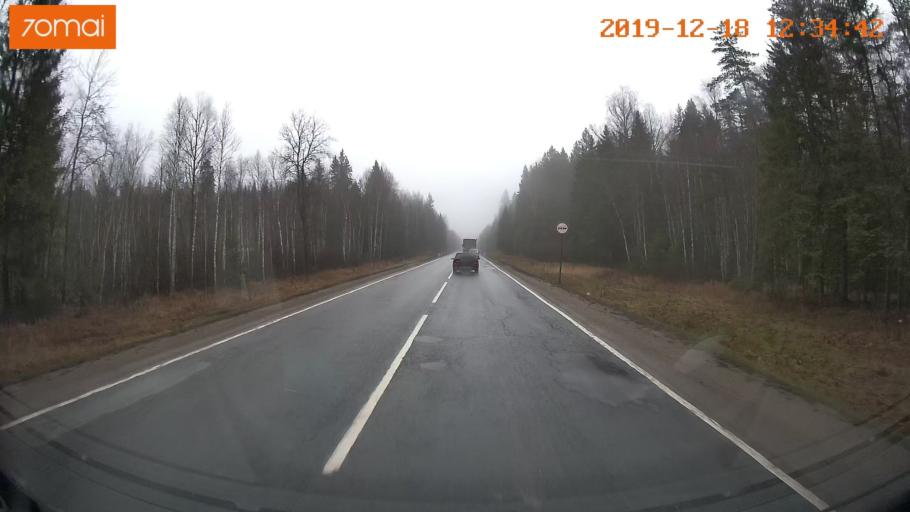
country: RU
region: Moskovskaya
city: Rumyantsevo
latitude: 56.1232
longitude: 36.5748
